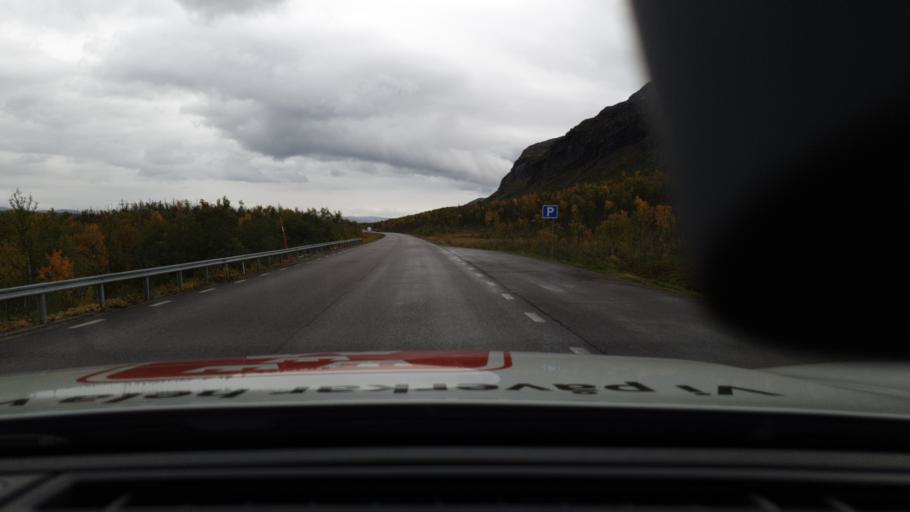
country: NO
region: Troms
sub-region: Bardu
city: Setermoen
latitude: 68.4264
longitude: 18.3536
